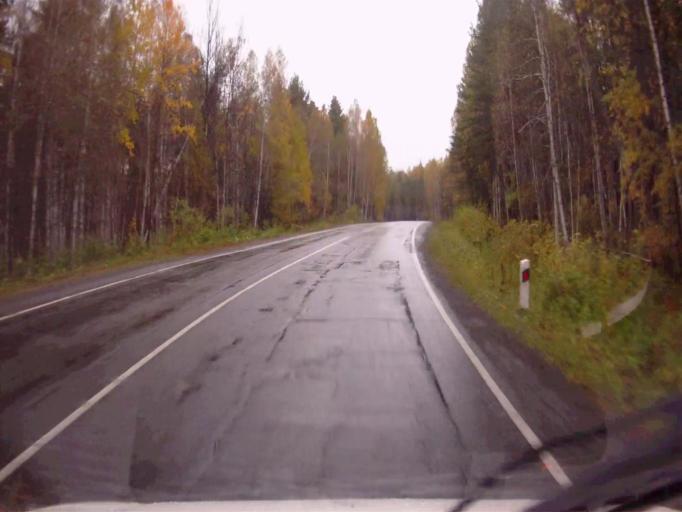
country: RU
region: Chelyabinsk
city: Verkhniy Ufaley
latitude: 55.9625
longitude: 60.3810
